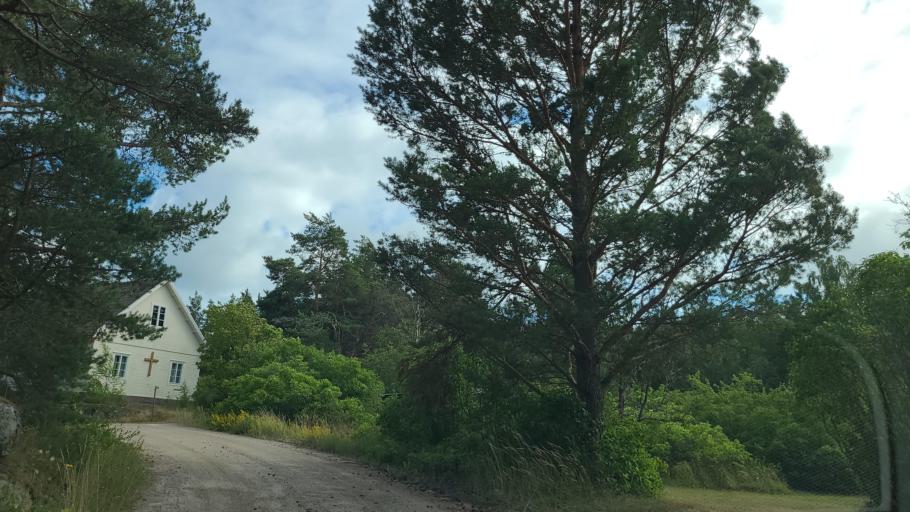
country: FI
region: Varsinais-Suomi
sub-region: Aboland-Turunmaa
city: Nagu
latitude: 60.1384
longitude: 21.8089
